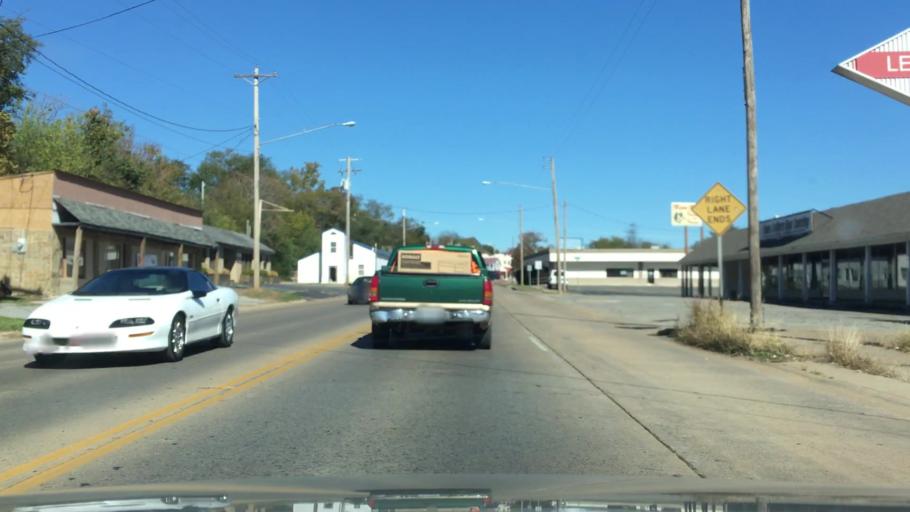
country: US
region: Oklahoma
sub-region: Cherokee County
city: Tahlequah
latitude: 35.9047
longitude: -94.9744
